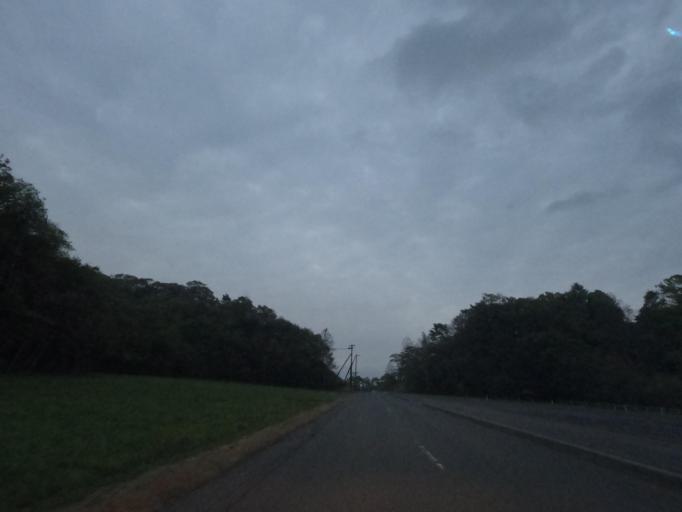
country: JP
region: Hokkaido
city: Date
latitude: 42.5584
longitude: 140.7962
